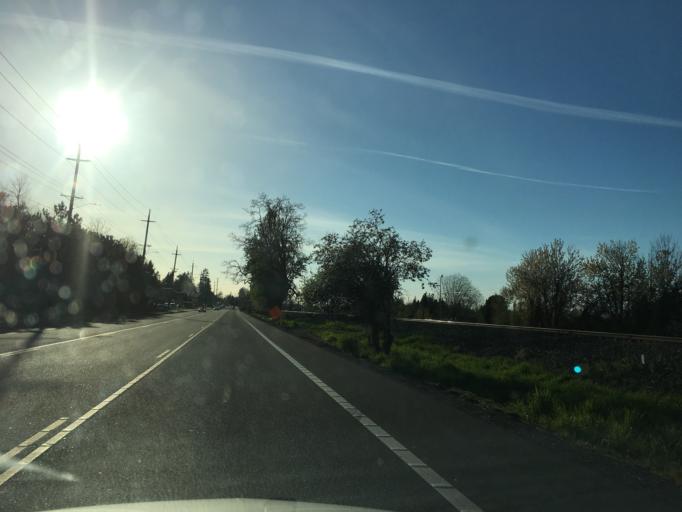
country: US
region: Oregon
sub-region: Multnomah County
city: Lents
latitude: 45.5561
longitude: -122.5309
